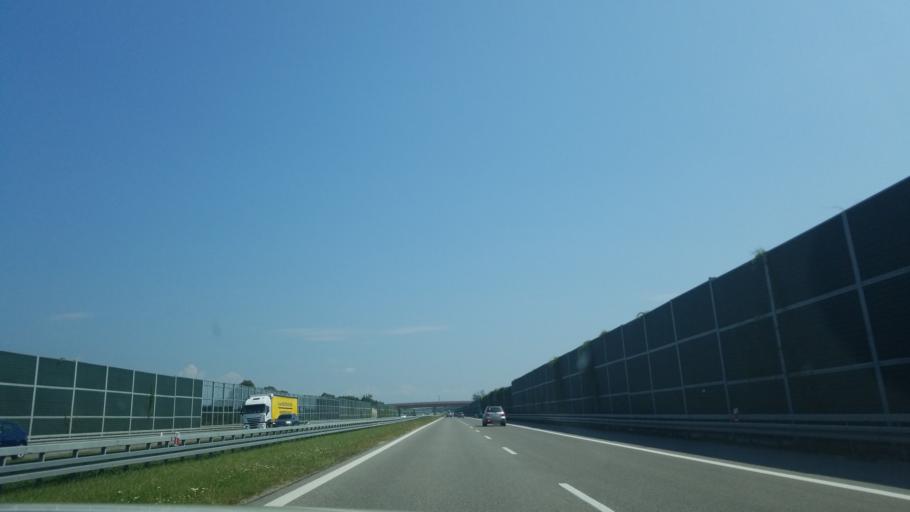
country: PL
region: Subcarpathian Voivodeship
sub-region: Powiat ropczycko-sedziszowski
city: Sedziszow Malopolski
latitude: 50.1147
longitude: 21.7276
